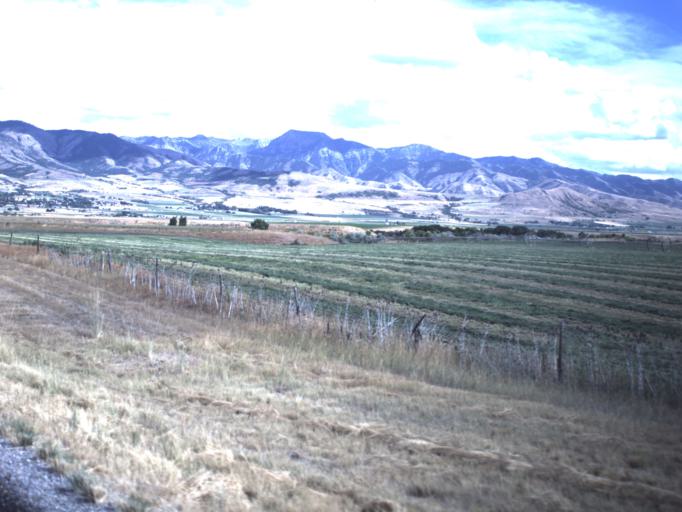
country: US
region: Utah
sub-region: Cache County
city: Lewiston
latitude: 41.9250
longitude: -111.8675
